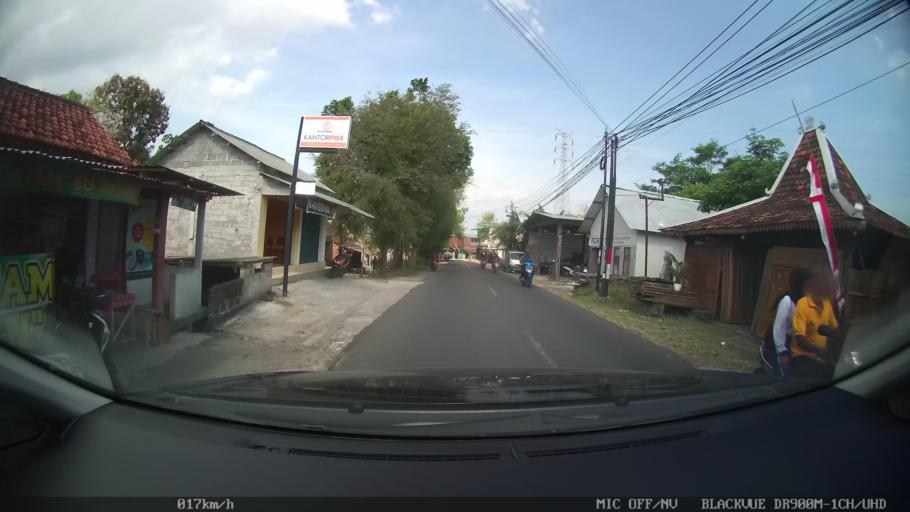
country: ID
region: Daerah Istimewa Yogyakarta
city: Kasihan
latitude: -7.8395
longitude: 110.3223
